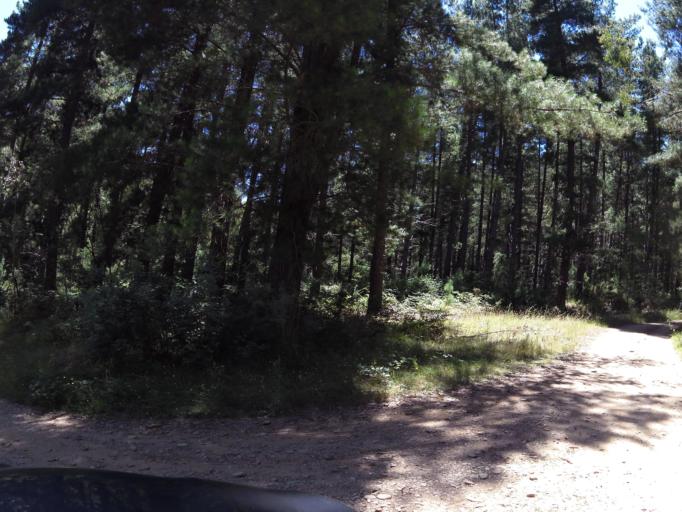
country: AU
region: Victoria
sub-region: Alpine
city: Mount Beauty
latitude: -36.7264
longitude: 146.9864
